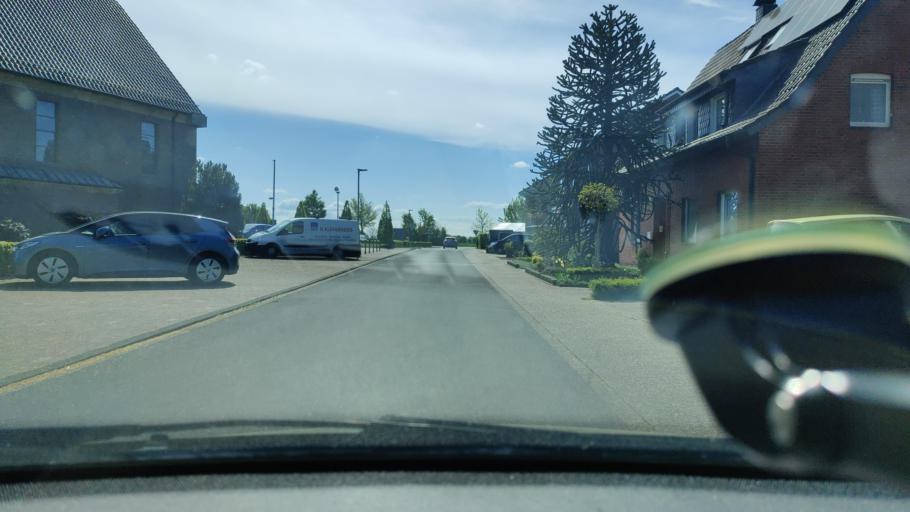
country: DE
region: North Rhine-Westphalia
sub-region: Regierungsbezirk Dusseldorf
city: Bocholt
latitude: 51.8632
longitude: 6.5616
